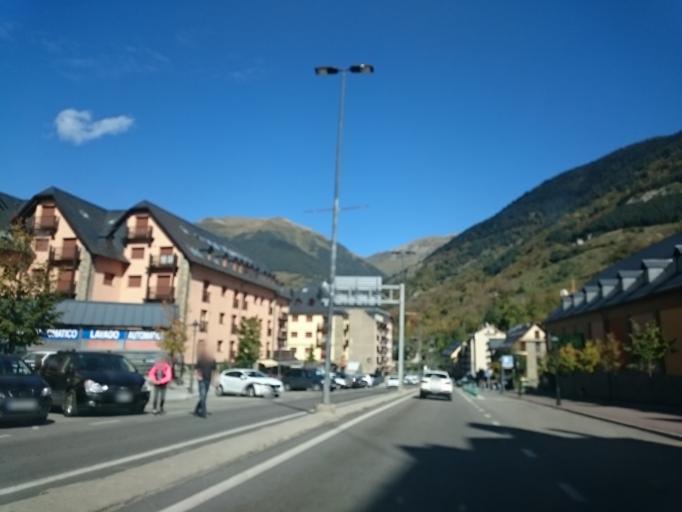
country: ES
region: Catalonia
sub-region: Provincia de Lleida
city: Vielha
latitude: 42.7033
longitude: 0.7936
